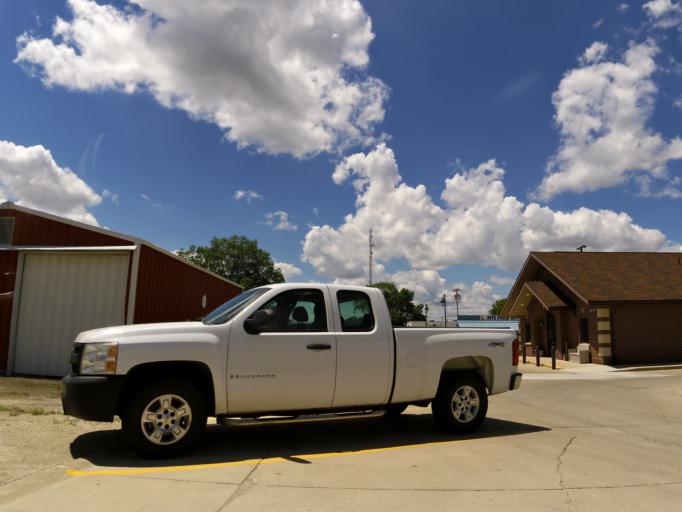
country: US
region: Iowa
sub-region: Fayette County
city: Oelwein
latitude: 42.6747
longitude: -91.9128
